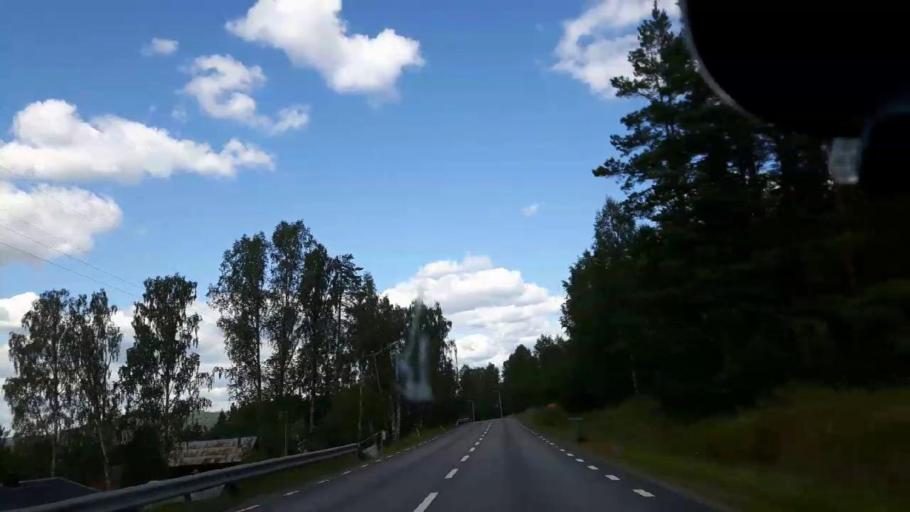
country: SE
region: Jaemtland
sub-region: Ragunda Kommun
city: Hammarstrand
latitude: 63.0010
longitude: 16.6757
